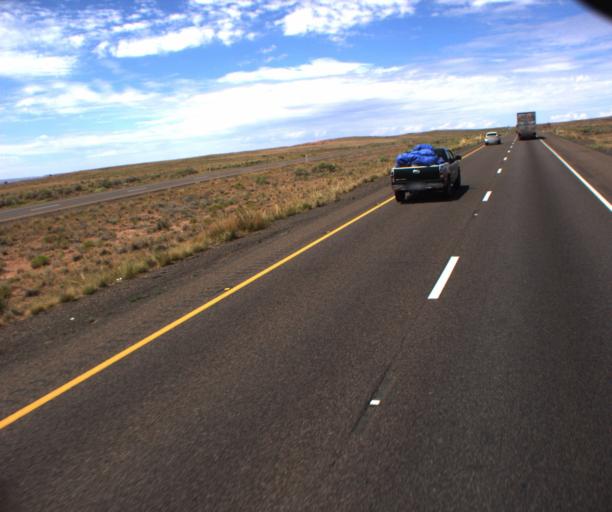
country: US
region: Arizona
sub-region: Navajo County
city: Holbrook
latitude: 35.0750
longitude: -109.7401
